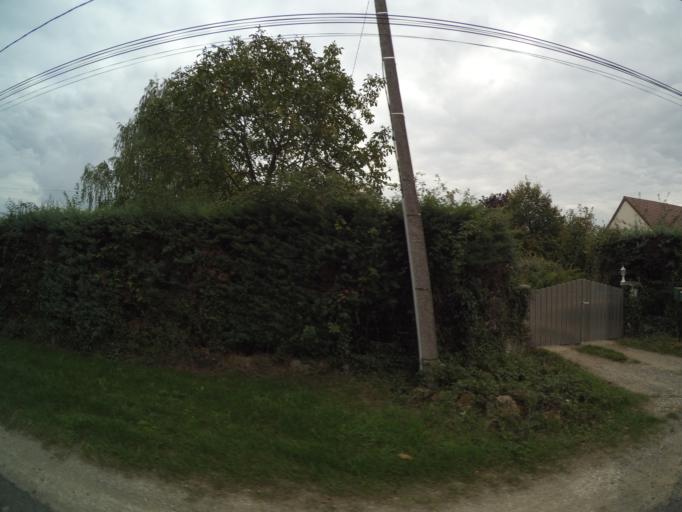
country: FR
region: Centre
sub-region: Departement d'Indre-et-Loire
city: Auzouer-en-Touraine
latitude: 47.5143
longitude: 0.9426
